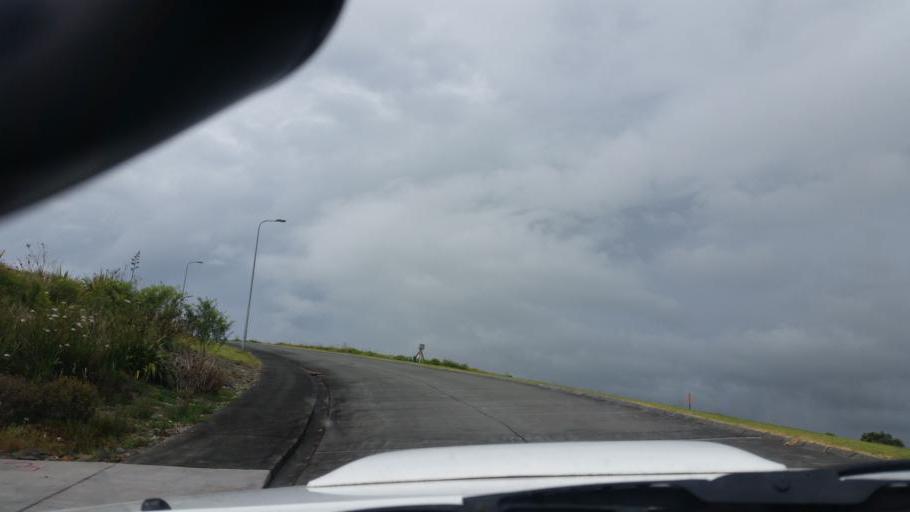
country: NZ
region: Auckland
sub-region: Auckland
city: Wellsford
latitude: -36.1550
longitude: 174.2248
